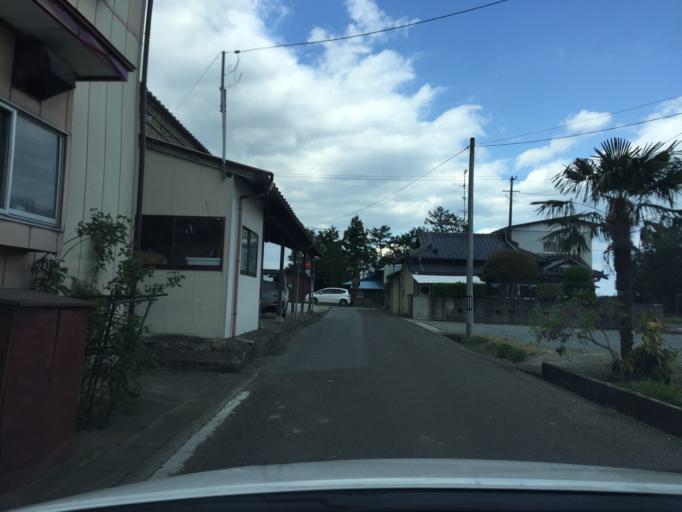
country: JP
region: Miyagi
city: Marumori
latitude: 37.7558
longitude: 140.9358
